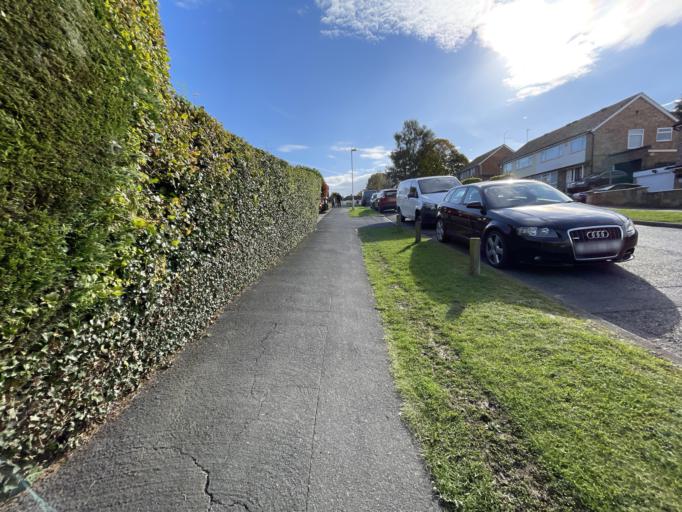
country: GB
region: England
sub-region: West Berkshire
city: Tilehurst
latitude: 51.4566
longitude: -1.0472
